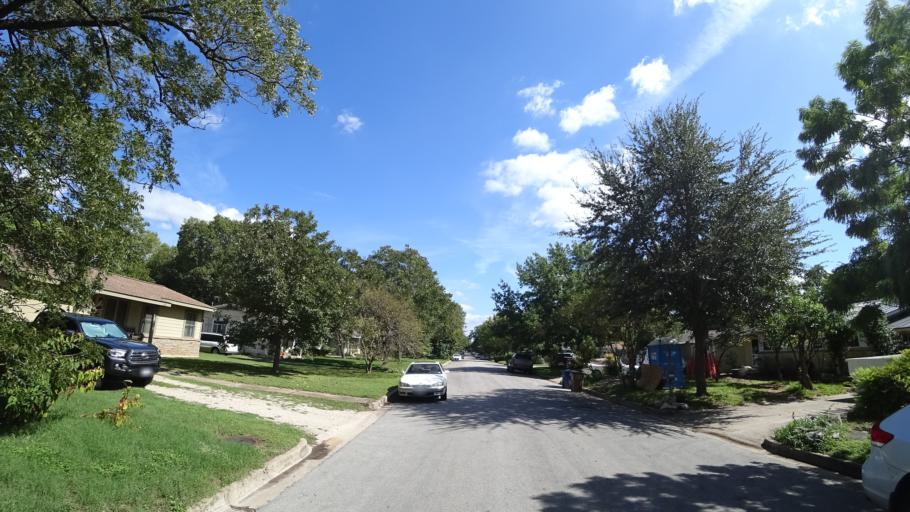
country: US
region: Texas
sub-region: Travis County
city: Austin
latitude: 30.3482
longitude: -97.7273
